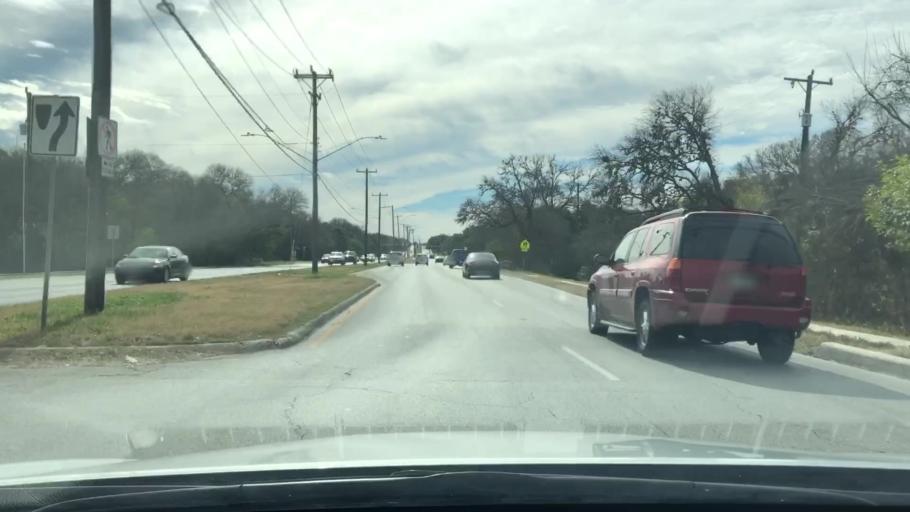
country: US
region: Texas
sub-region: Bexar County
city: Terrell Hills
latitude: 29.5091
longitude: -98.4346
